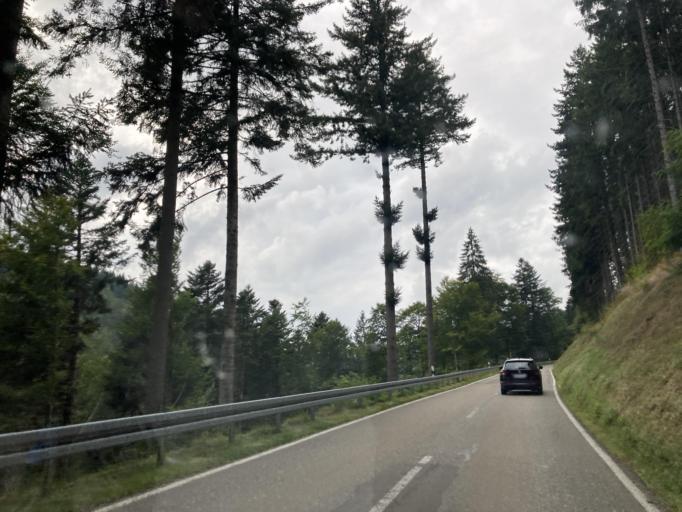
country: DE
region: Baden-Wuerttemberg
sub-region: Freiburg Region
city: Bollen
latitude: 47.7906
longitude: 7.8178
